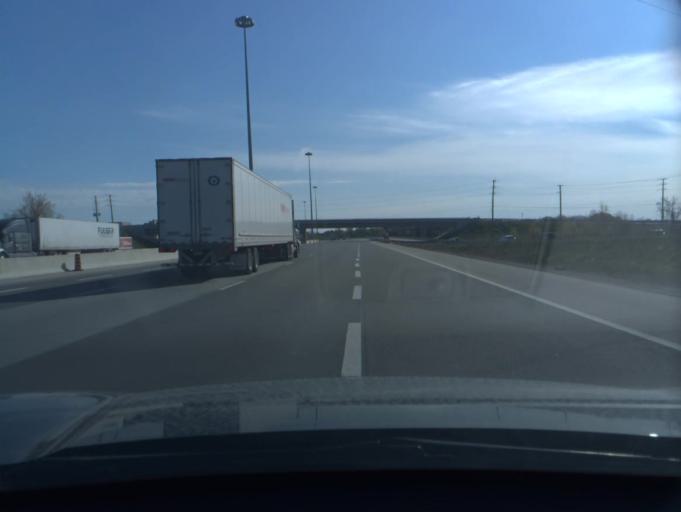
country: CA
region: Ontario
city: North Perth
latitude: 43.8088
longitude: -80.9998
